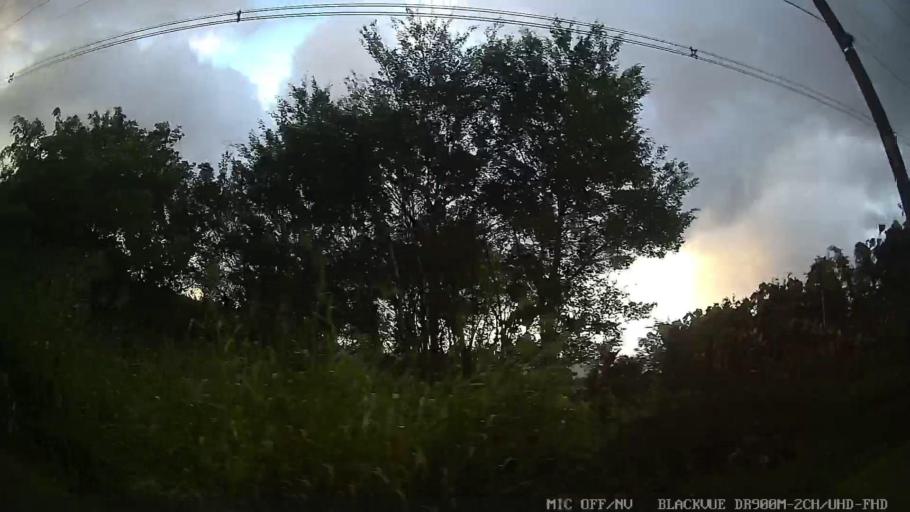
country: BR
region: Sao Paulo
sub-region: Itanhaem
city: Itanhaem
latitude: -24.0986
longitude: -46.8019
